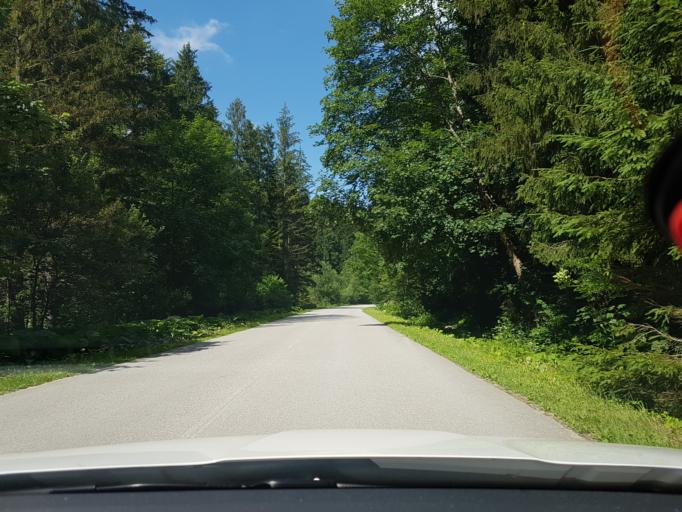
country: SK
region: Zilinsky
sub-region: Okres Zilina
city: Terchova
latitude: 49.2324
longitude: 19.0556
